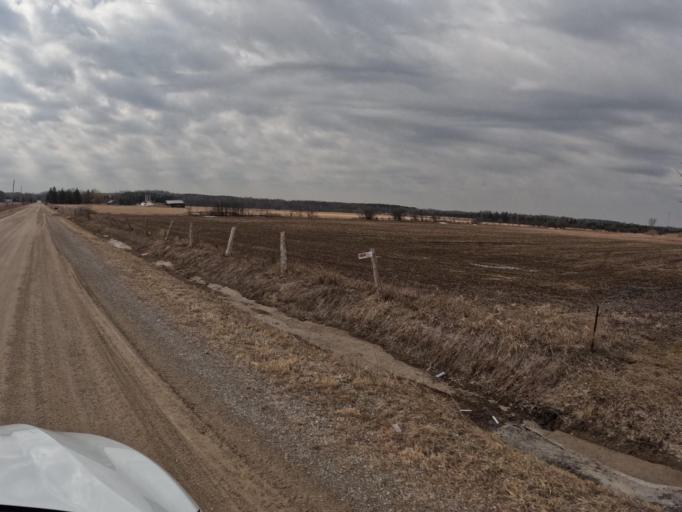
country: CA
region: Ontario
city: Orangeville
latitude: 43.9062
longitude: -80.2146
